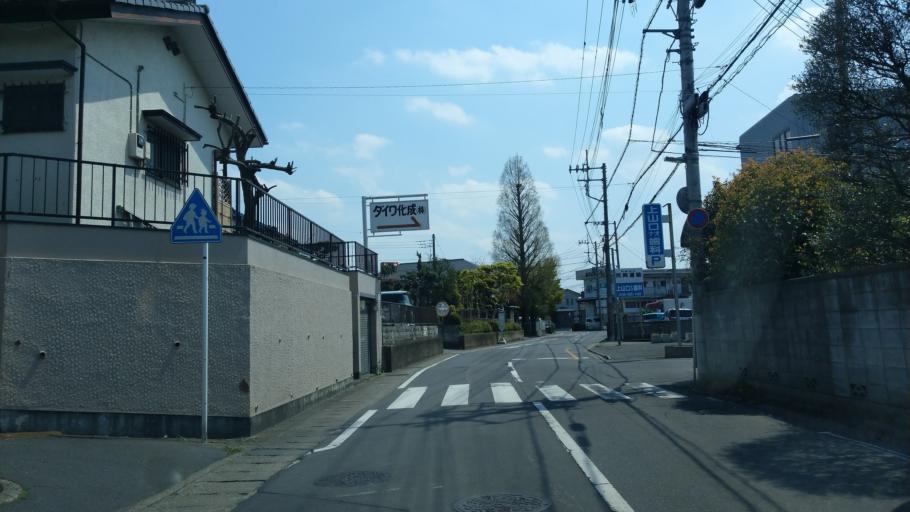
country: JP
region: Saitama
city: Saitama
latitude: 35.9000
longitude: 139.6520
